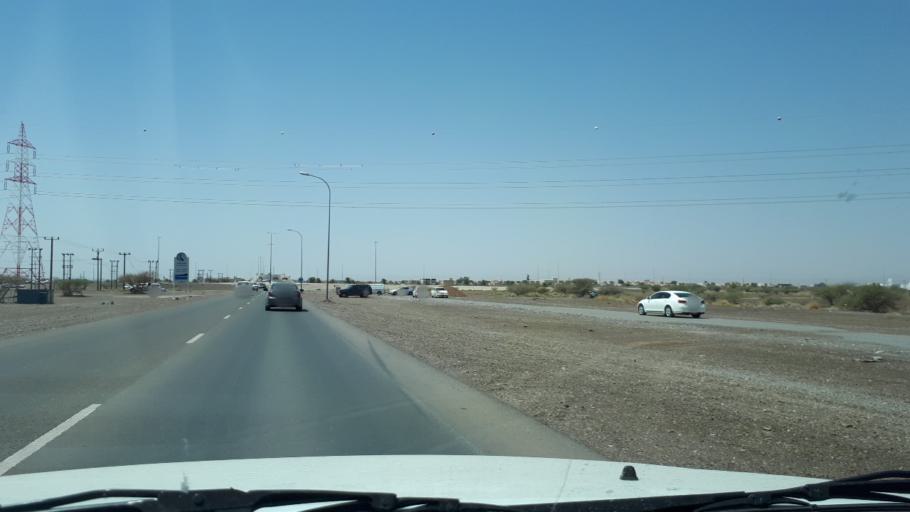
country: OM
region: Muhafazat ad Dakhiliyah
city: Bahla'
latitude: 22.9322
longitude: 57.2572
